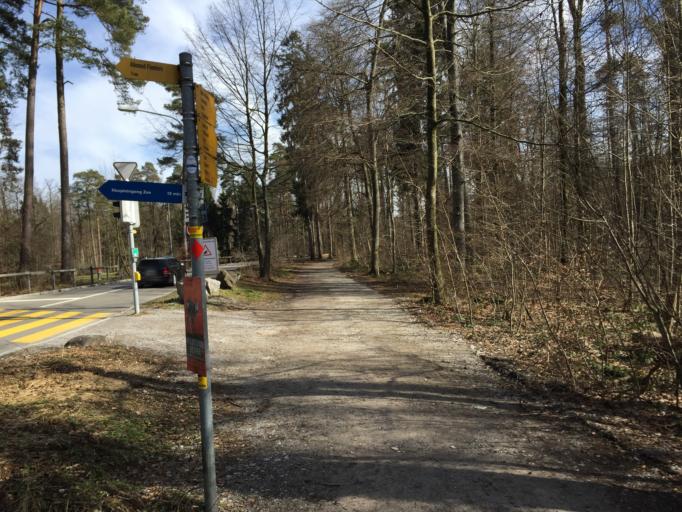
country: CH
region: Zurich
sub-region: Bezirk Zuerich
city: Zuerich (Kreis 7)
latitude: 47.3785
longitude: 8.5751
